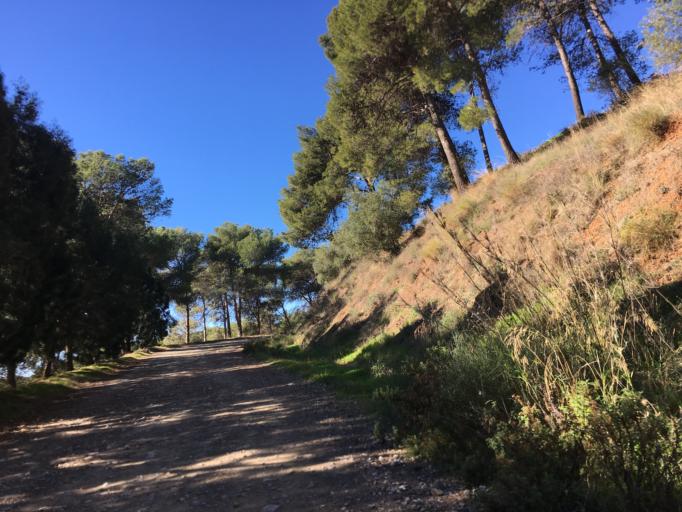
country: ES
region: Andalusia
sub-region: Provincia de Malaga
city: Malaga
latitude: 36.7800
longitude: -4.3854
